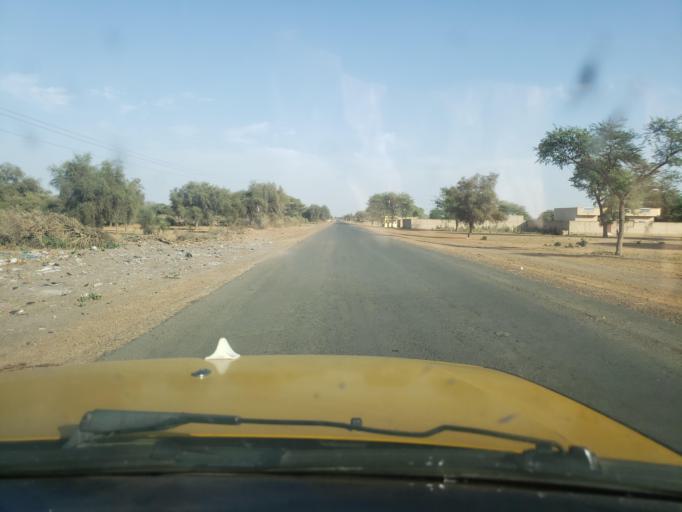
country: SN
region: Louga
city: Louga
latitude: 15.5016
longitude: -15.9410
